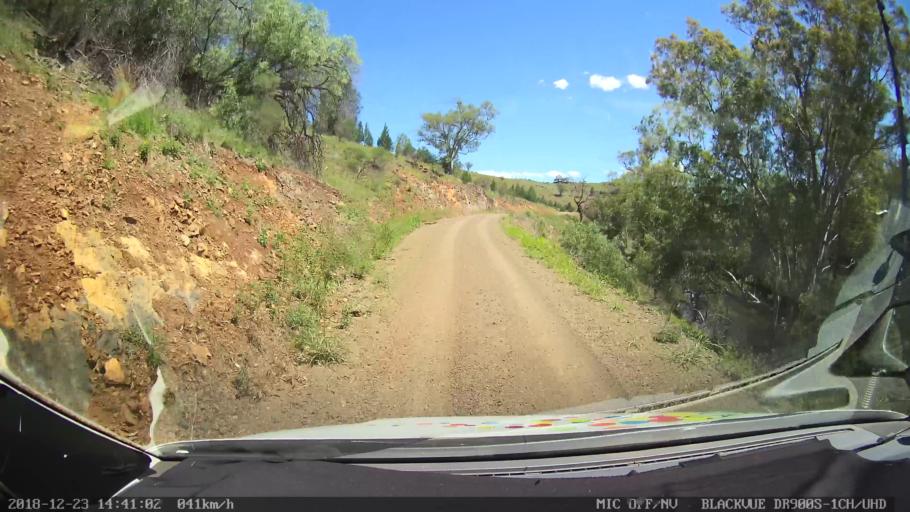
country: AU
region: New South Wales
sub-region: Tamworth Municipality
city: Manilla
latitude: -30.6292
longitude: 150.9028
